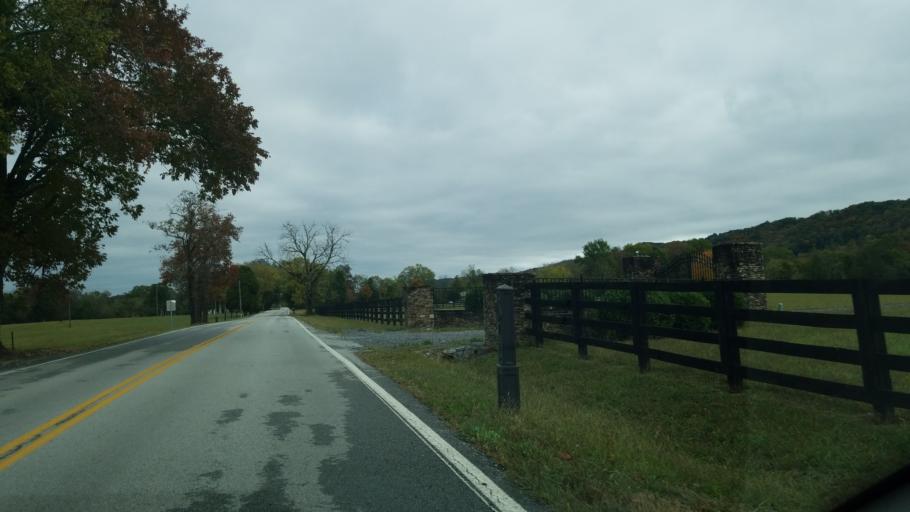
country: US
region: Tennessee
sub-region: Hamilton County
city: Lakesite
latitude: 35.2017
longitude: -85.0127
